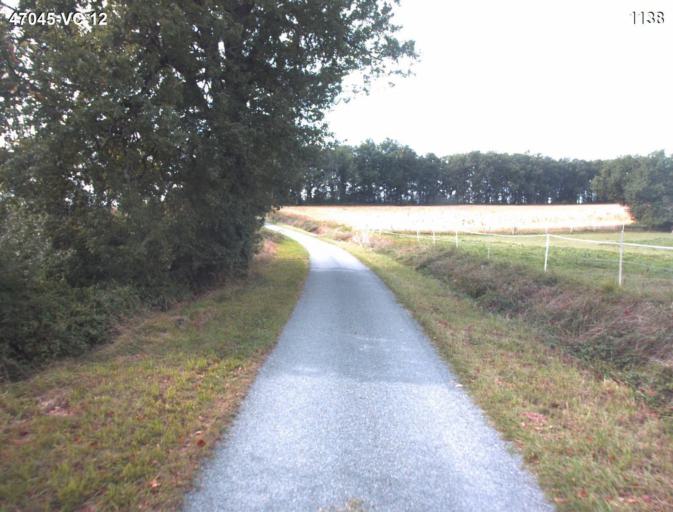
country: FR
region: Aquitaine
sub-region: Departement du Lot-et-Garonne
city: Nerac
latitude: 44.1447
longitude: 0.4281
